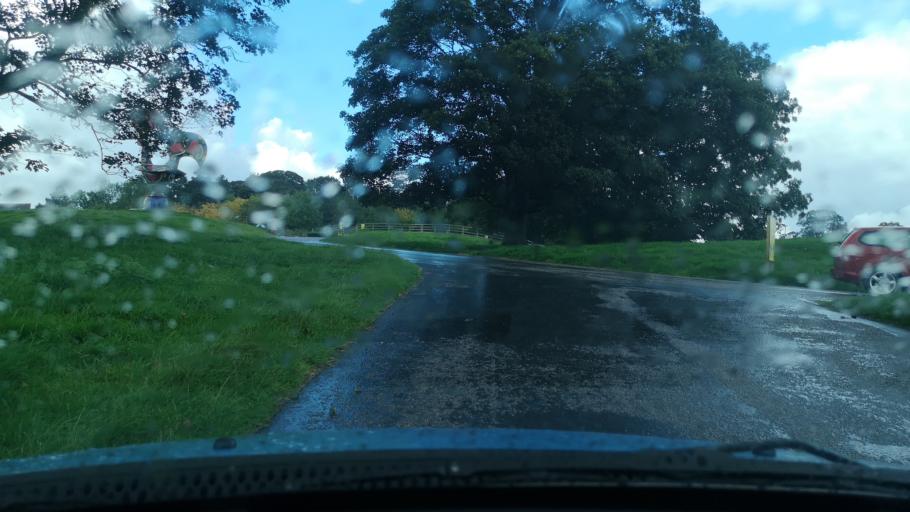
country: GB
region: England
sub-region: City and Borough of Wakefield
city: Crigglestone
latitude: 53.6132
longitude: -1.5663
